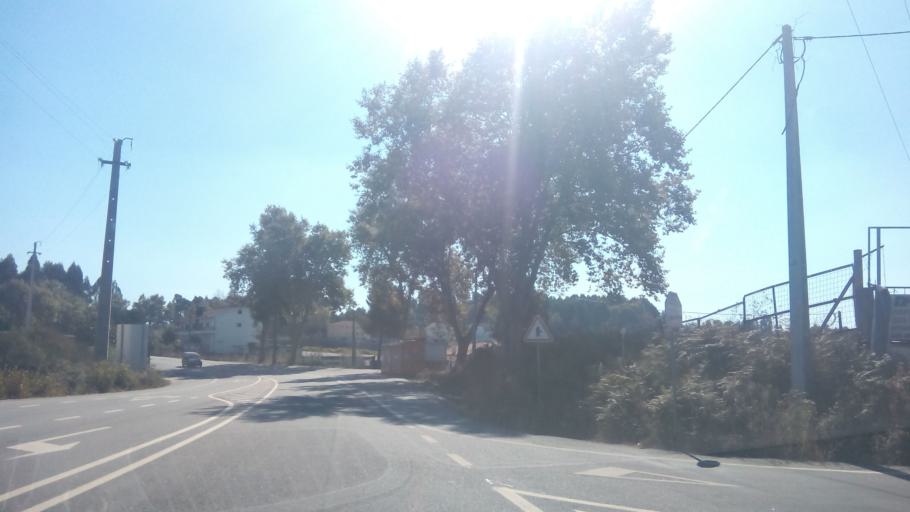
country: PT
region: Porto
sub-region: Lousada
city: Meinedo
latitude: 41.2462
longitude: -8.2160
